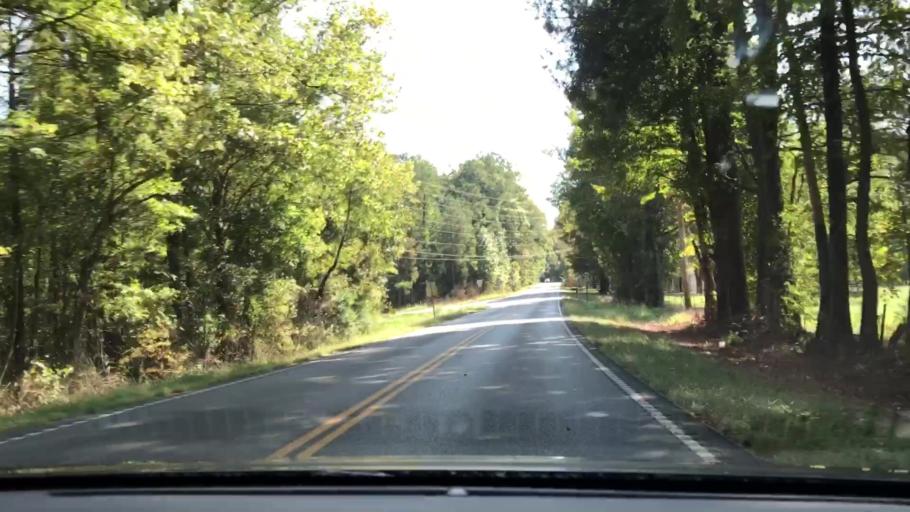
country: US
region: Kentucky
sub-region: Marshall County
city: Benton
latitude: 36.7679
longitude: -88.2748
